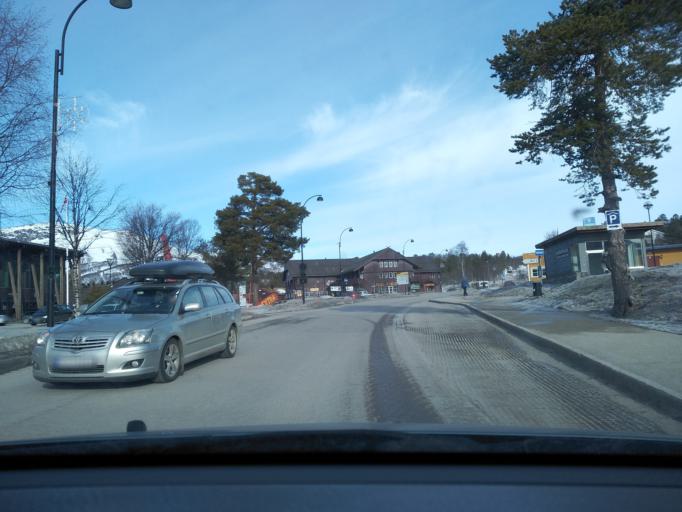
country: NO
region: Aust-Agder
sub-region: Bykle
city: Hovden
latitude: 59.5595
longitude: 7.3567
